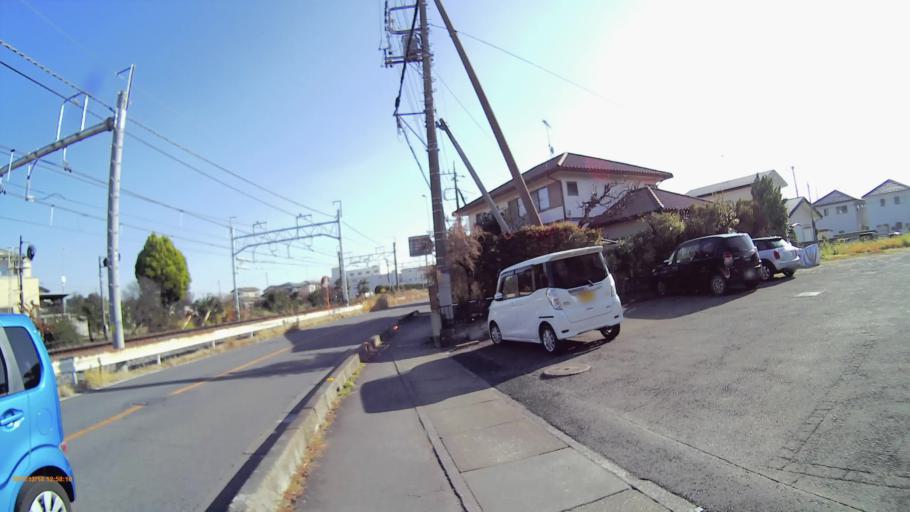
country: JP
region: Saitama
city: Fukiage-fujimi
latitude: 36.1000
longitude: 139.4598
